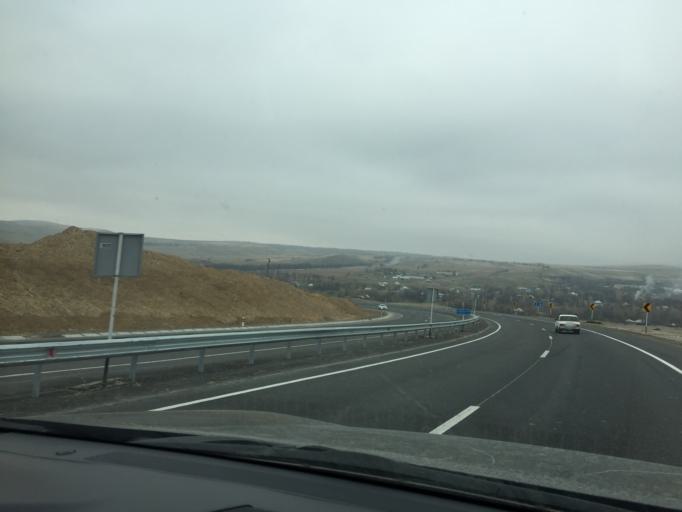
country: KZ
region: Ongtustik Qazaqstan
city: Sastobe
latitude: 42.4925
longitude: 69.9577
